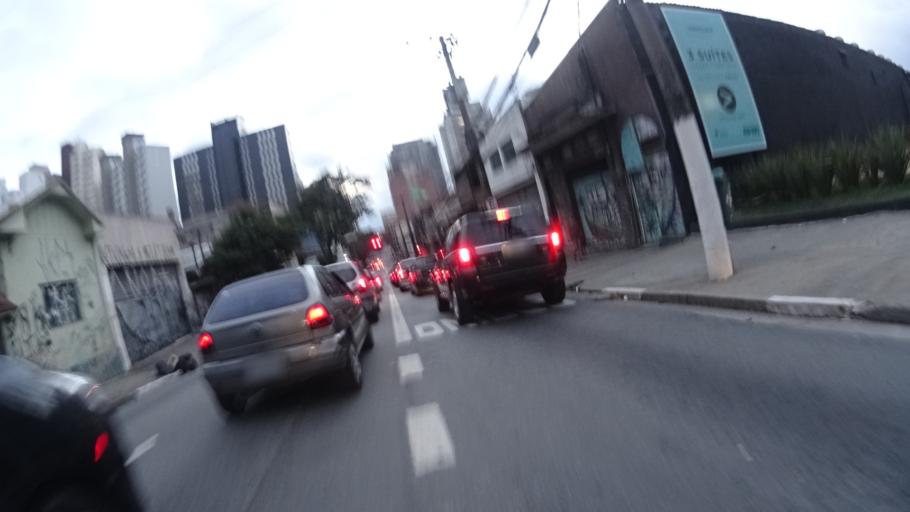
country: BR
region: Sao Paulo
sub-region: Sao Paulo
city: Sao Paulo
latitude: -23.5605
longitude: -46.6863
